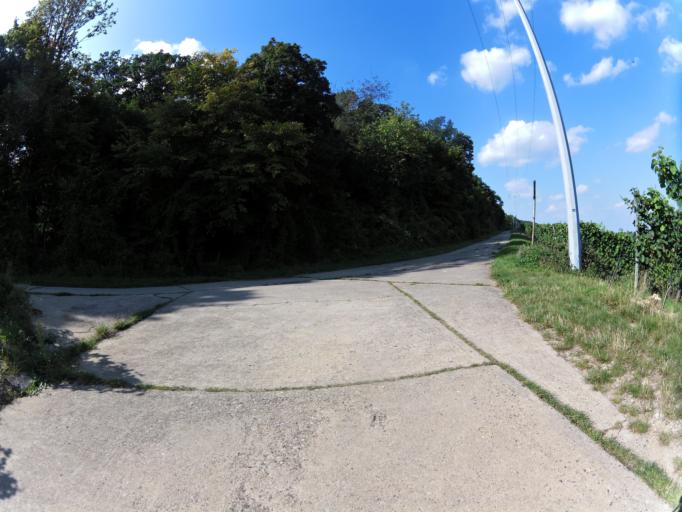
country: DE
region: Bavaria
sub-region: Regierungsbezirk Unterfranken
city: Nordheim
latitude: 49.8481
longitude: 10.1647
